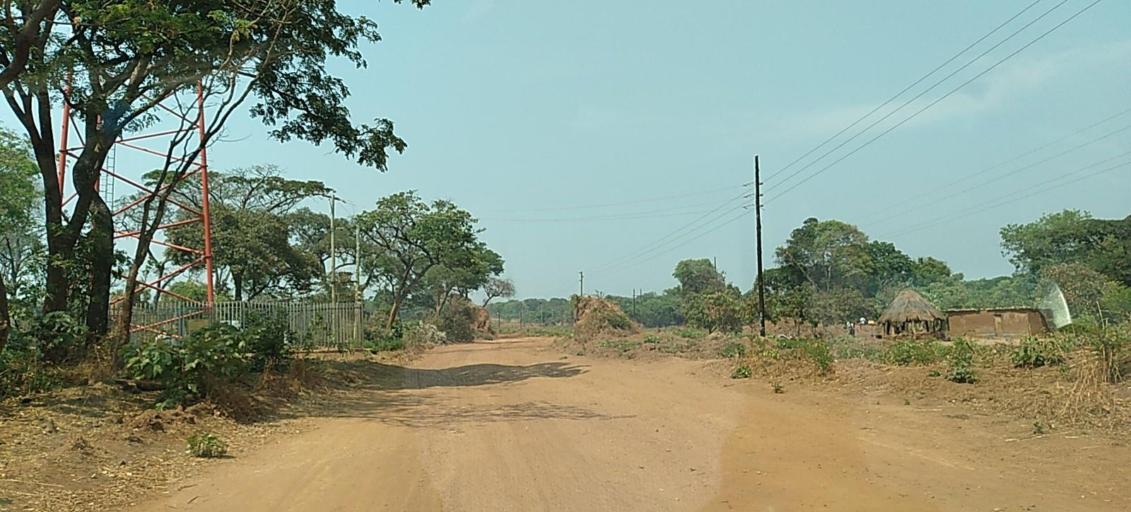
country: ZM
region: Copperbelt
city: Chingola
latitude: -13.0467
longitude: 27.4326
